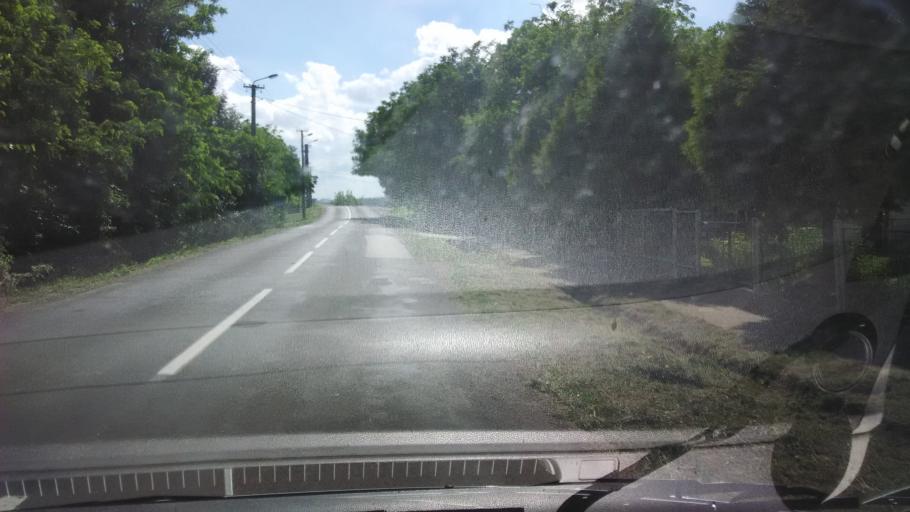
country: SK
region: Nitriansky
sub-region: Okres Nitra
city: Vrable
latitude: 48.1495
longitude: 18.4198
